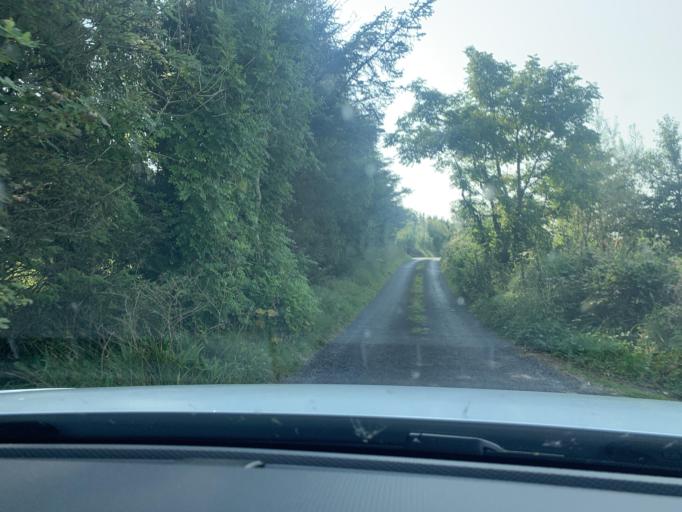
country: IE
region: Connaught
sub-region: Maigh Eo
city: Ballyhaunis
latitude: 53.7910
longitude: -8.7395
